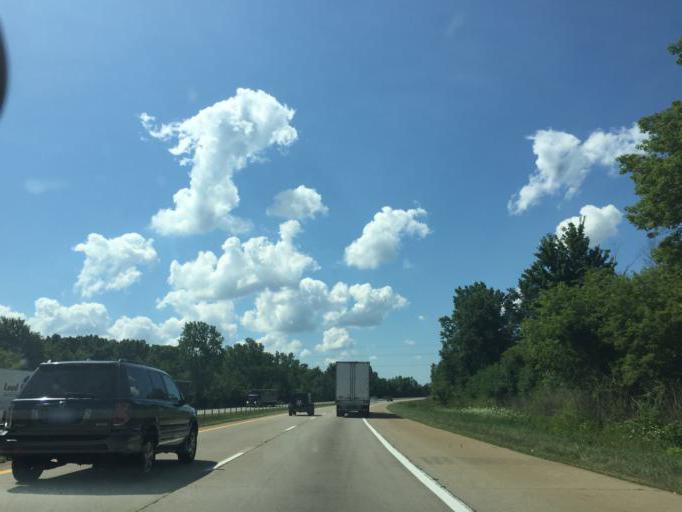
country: US
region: Michigan
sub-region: Monroe County
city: Lambertville
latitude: 41.8068
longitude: -83.6838
